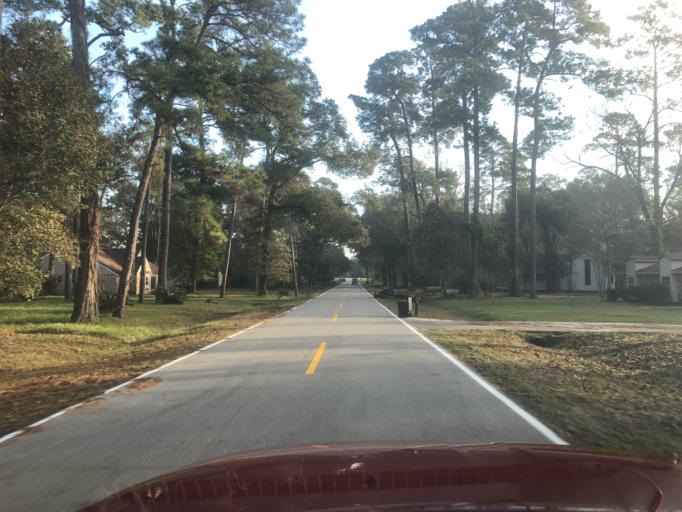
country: US
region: Texas
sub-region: Harris County
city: Spring
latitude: 30.0189
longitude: -95.4760
